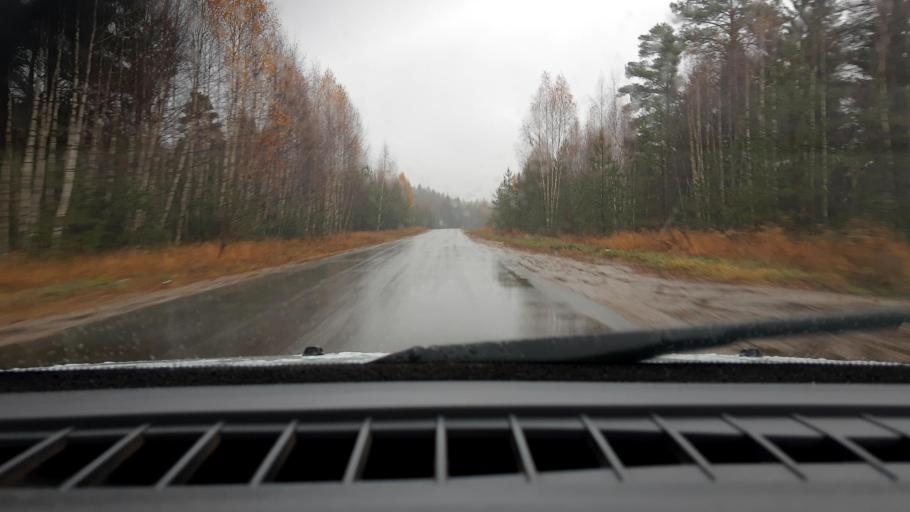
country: RU
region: Nizjnij Novgorod
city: Linda
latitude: 56.6944
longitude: 44.2052
